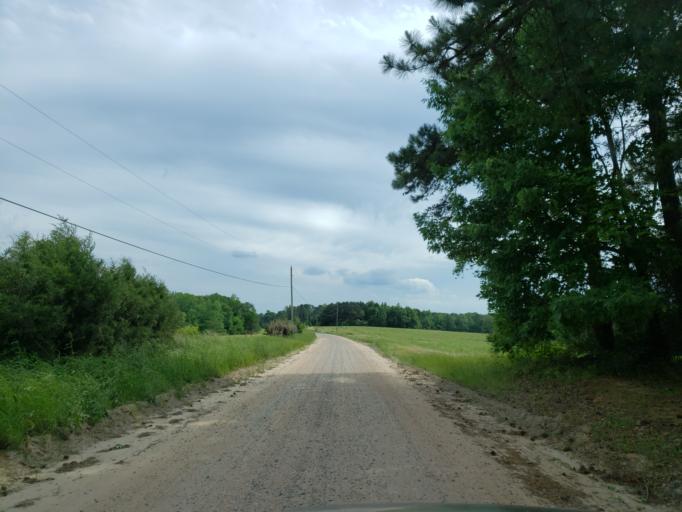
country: US
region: Georgia
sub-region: Monroe County
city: Forsyth
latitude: 32.9774
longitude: -83.9136
